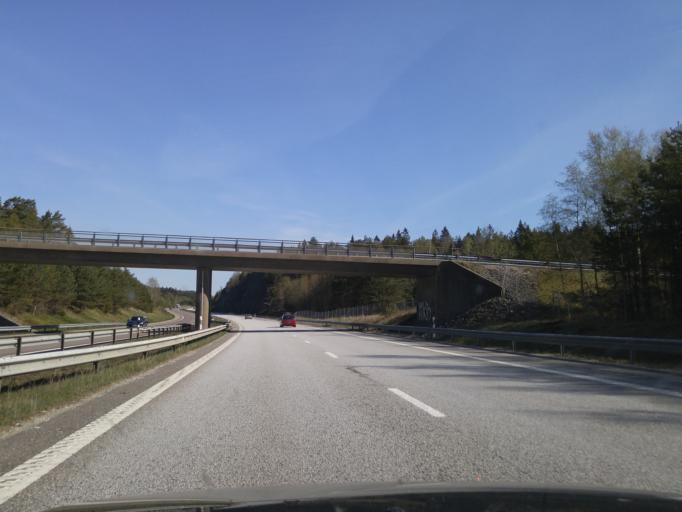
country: SE
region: Vaestra Goetaland
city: Svanesund
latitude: 58.1532
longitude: 11.8869
